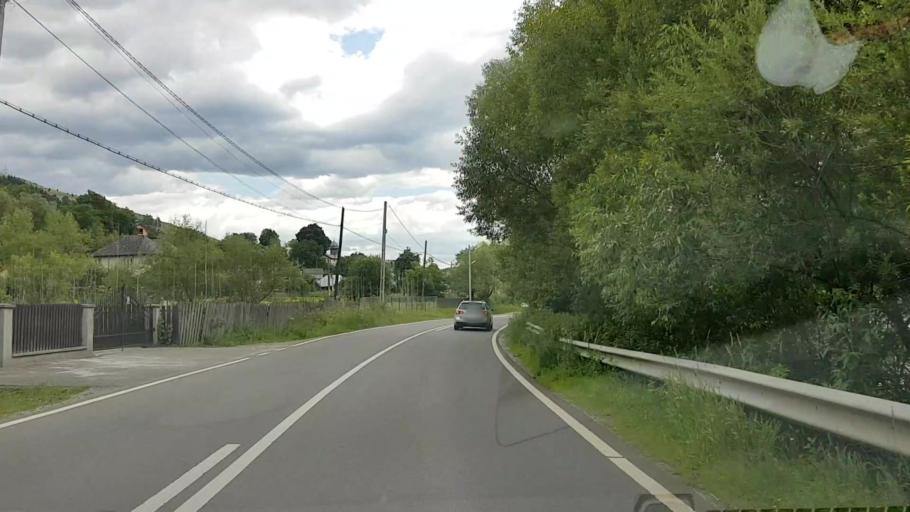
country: RO
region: Neamt
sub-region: Comuna Farcasa
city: Farcasa
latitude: 47.1691
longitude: 25.8020
